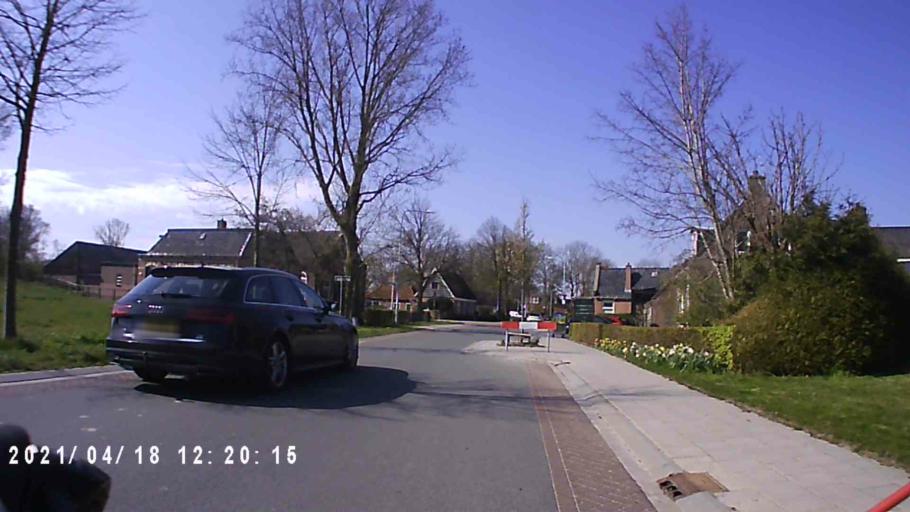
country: NL
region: Friesland
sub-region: Gemeente Kollumerland en Nieuwkruisland
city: Kollum
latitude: 53.3217
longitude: 6.1410
